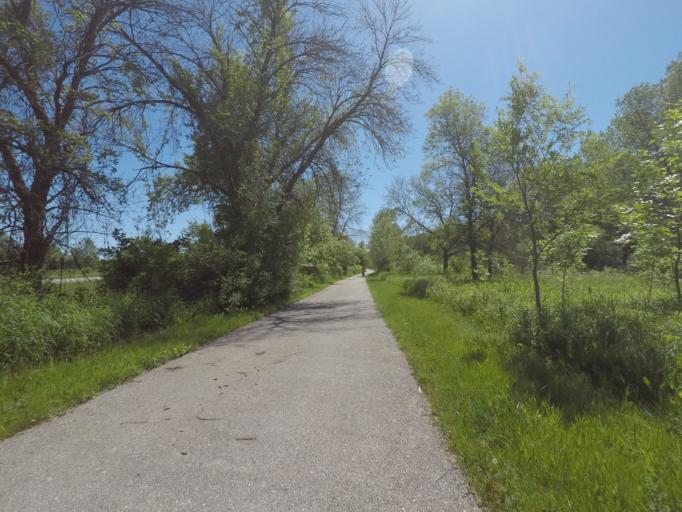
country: US
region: Wisconsin
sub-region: Sheboygan County
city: Kohler
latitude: 43.7530
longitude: -87.7729
